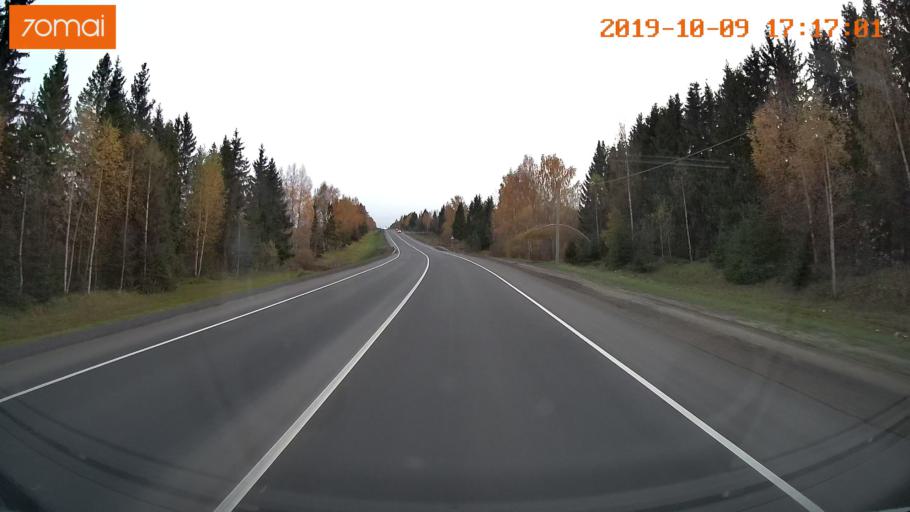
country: RU
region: Ivanovo
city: Furmanov
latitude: 57.2815
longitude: 41.1592
